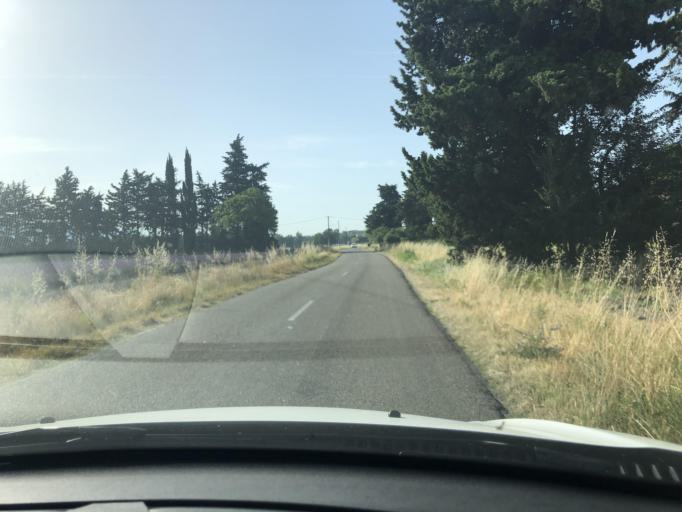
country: FR
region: Provence-Alpes-Cote d'Azur
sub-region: Departement du Vaucluse
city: Velleron
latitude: 43.9648
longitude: 5.0193
